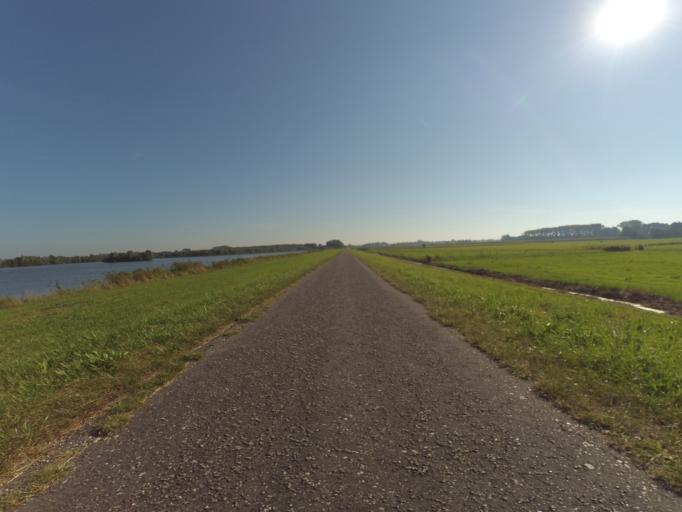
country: NL
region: Gelderland
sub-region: Gemeente Nijkerk
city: Nijkerk
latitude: 52.2639
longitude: 5.5164
